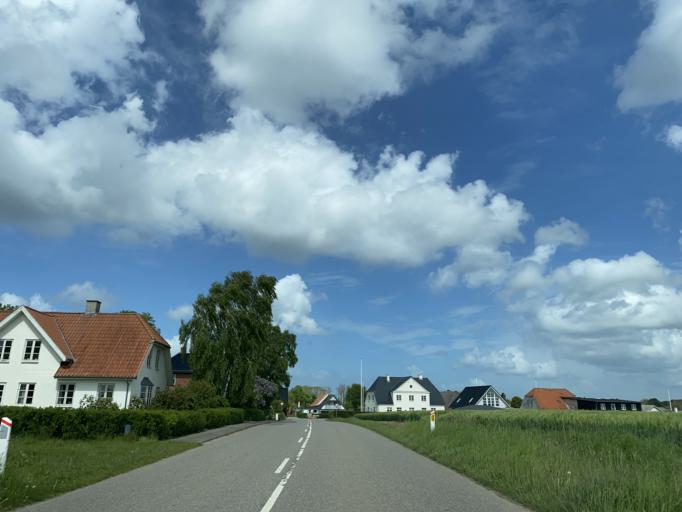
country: DK
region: South Denmark
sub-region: Sonderborg Kommune
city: Dybbol
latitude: 54.9736
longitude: 9.7140
